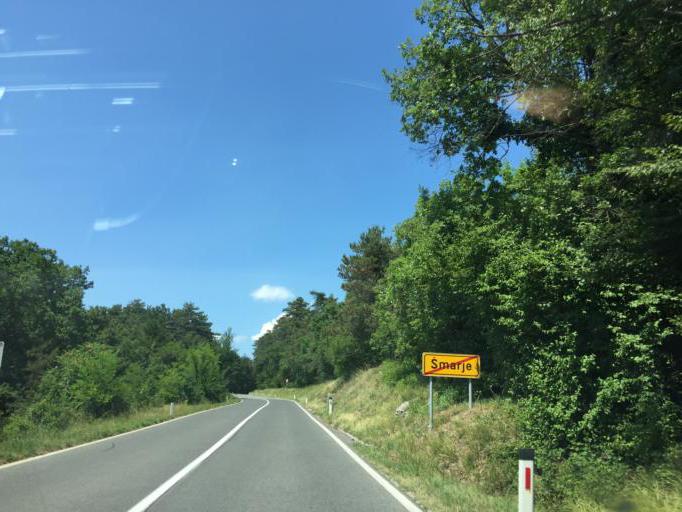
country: SI
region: Sezana
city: Sezana
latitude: 45.7277
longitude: 13.8688
